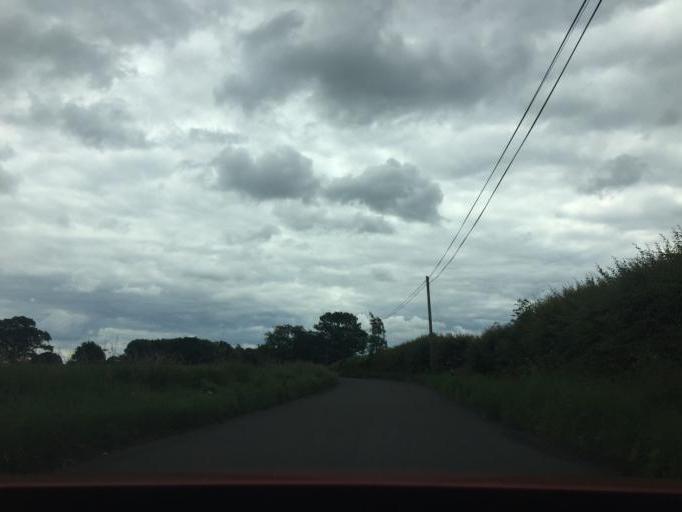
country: GB
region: England
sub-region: Hertfordshire
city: Harpenden
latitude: 51.8574
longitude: -0.3380
